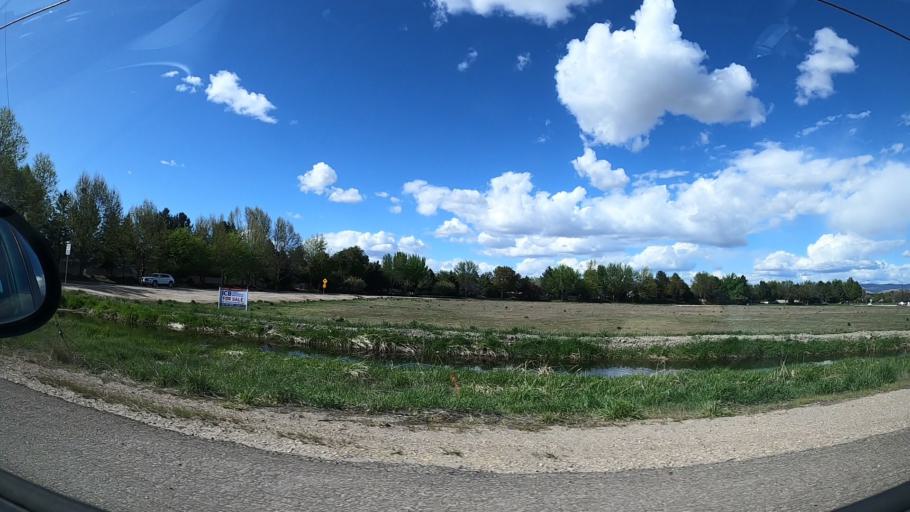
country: US
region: Idaho
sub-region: Ada County
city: Eagle
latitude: 43.6955
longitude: -116.3815
